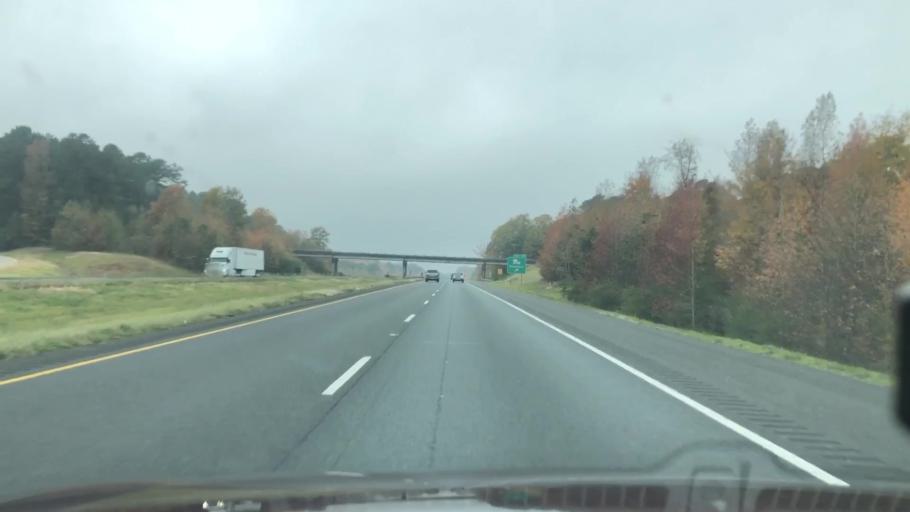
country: US
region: Louisiana
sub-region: Lincoln Parish
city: Grambling
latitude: 32.5486
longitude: -92.7848
